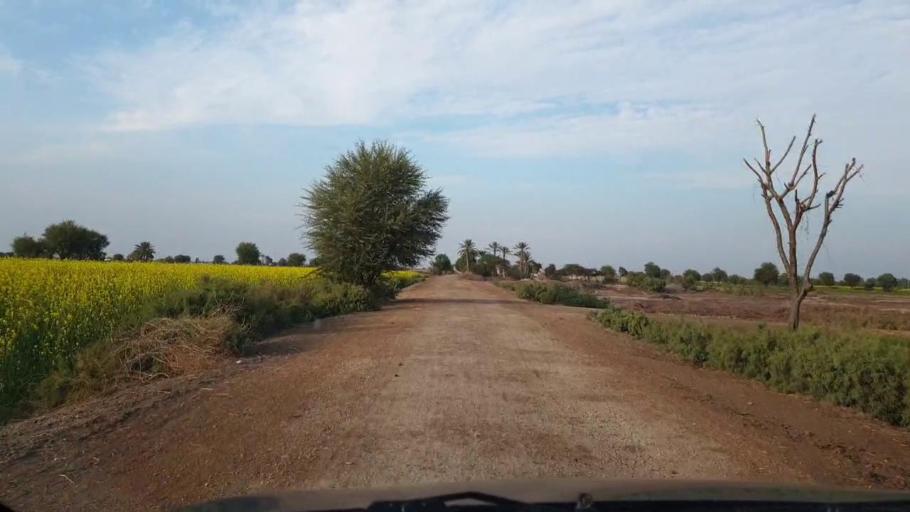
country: PK
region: Sindh
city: Jhol
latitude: 25.9757
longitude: 68.8737
